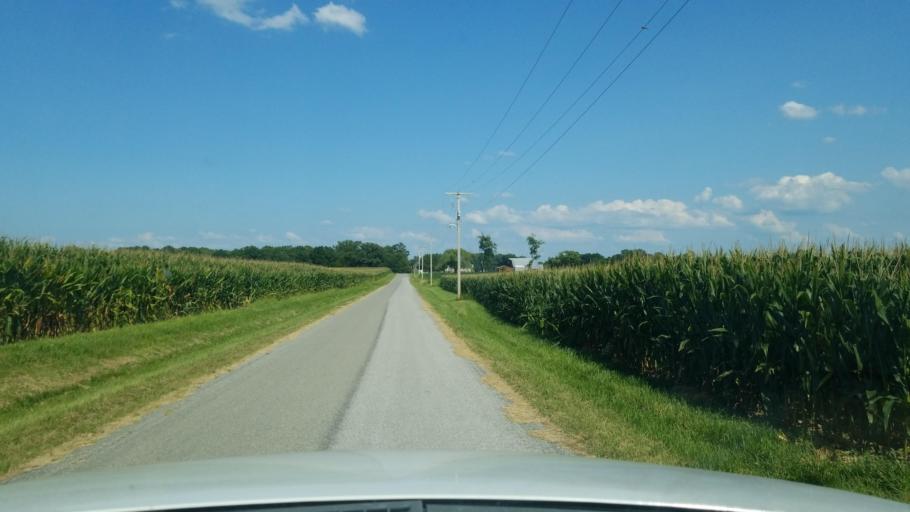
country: US
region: Illinois
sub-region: Saline County
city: Harrisburg
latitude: 37.7865
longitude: -88.4981
